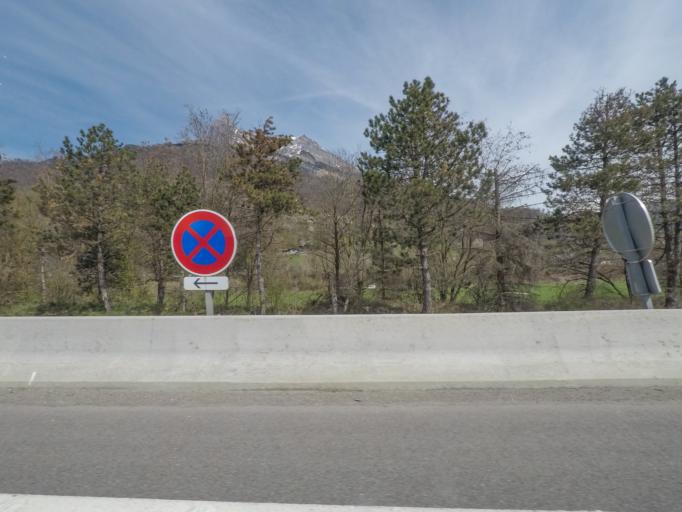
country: FR
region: Rhone-Alpes
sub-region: Departement de la Haute-Savoie
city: Passy
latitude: 45.9185
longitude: 6.6728
